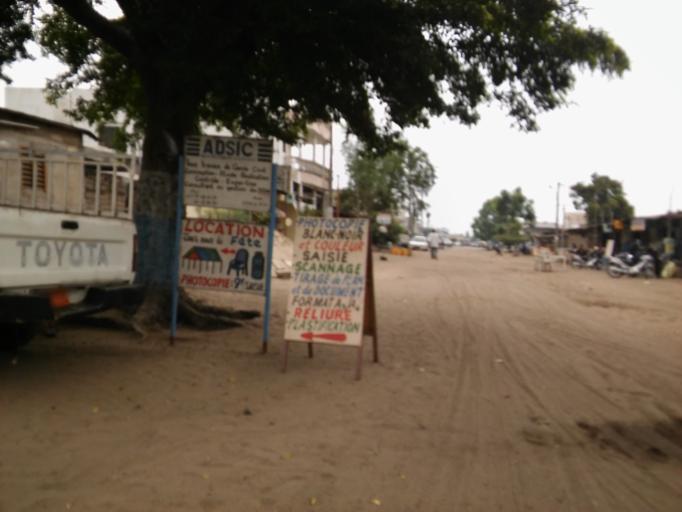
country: BJ
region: Littoral
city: Cotonou
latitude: 6.3882
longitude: 2.3725
